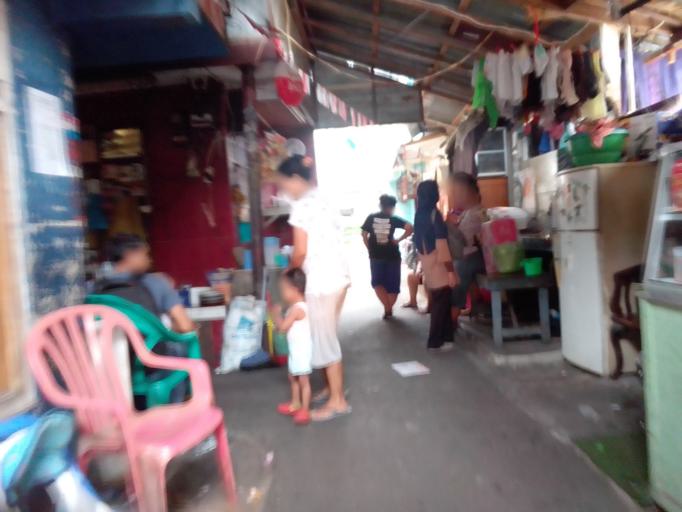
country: ID
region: Jakarta Raya
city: Jakarta
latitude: -6.1999
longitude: 106.8192
